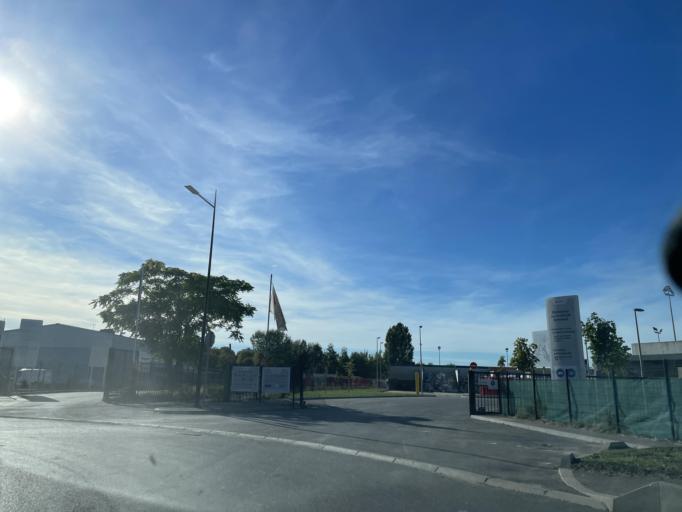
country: FR
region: Ile-de-France
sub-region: Departement du Val-de-Marne
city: Bonneuil-sur-Marne
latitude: 48.7807
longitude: 2.4836
